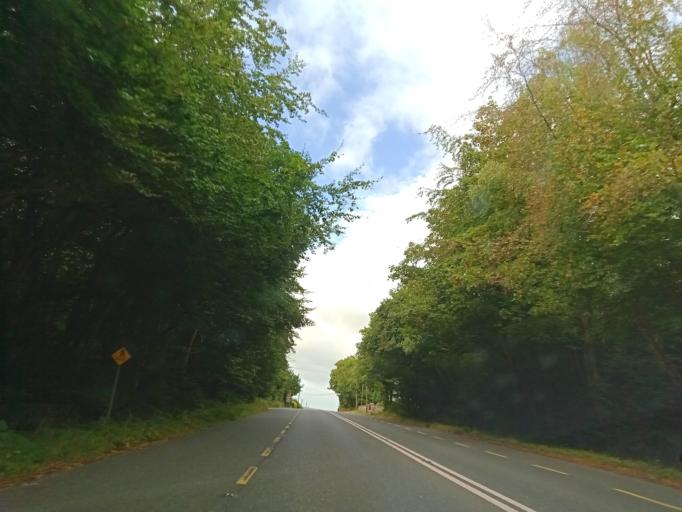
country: IE
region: Leinster
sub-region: Laois
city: Abbeyleix
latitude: 52.8371
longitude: -7.4223
